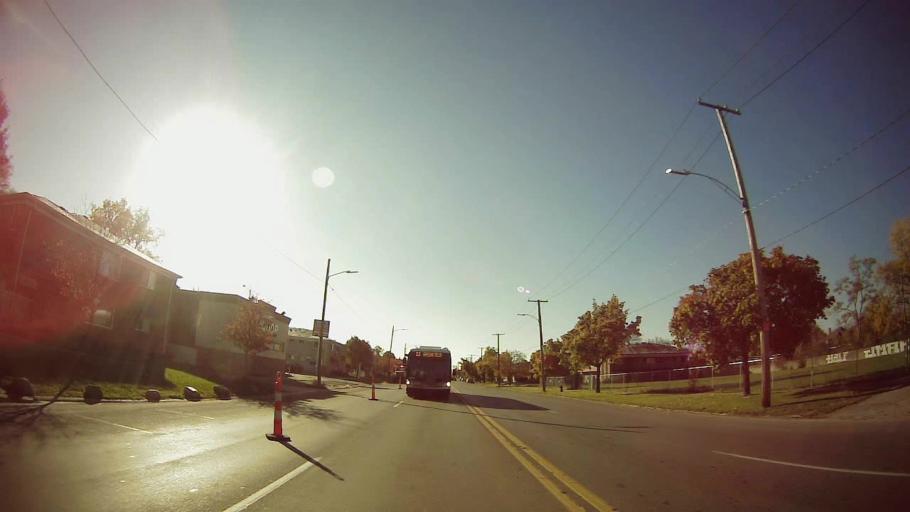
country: US
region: Michigan
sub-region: Oakland County
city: Oak Park
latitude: 42.3987
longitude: -83.1986
